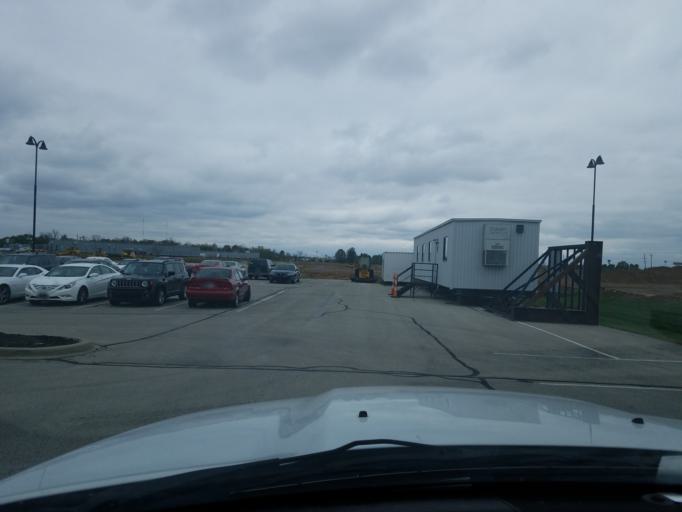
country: US
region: Indiana
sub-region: Clark County
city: Clarksville
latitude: 38.3287
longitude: -85.7479
